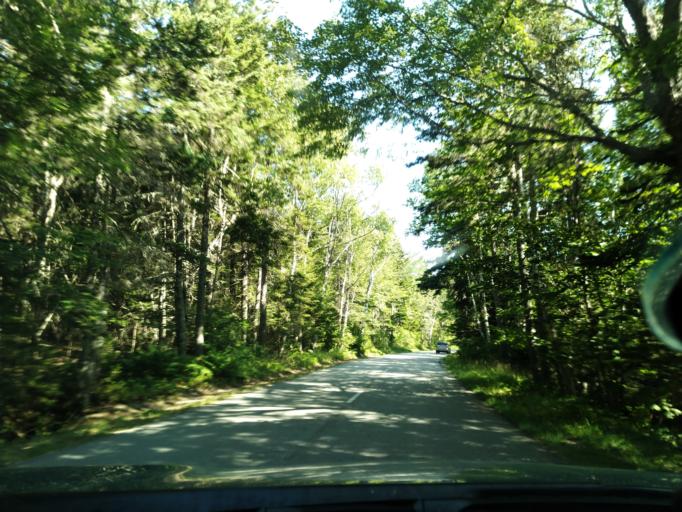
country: US
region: Maine
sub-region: Hancock County
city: Gouldsboro
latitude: 44.3539
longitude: -68.0476
